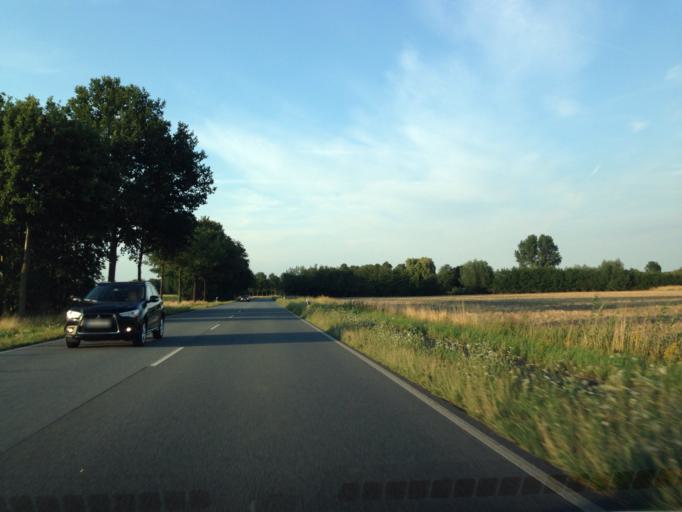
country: DE
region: North Rhine-Westphalia
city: Ludinghausen
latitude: 51.7951
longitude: 7.4714
